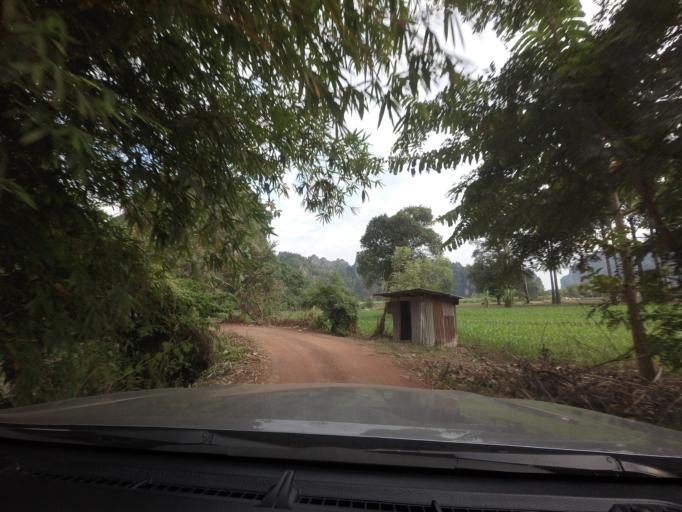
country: TH
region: Phitsanulok
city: Noen Maprang
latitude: 16.5831
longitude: 100.6850
